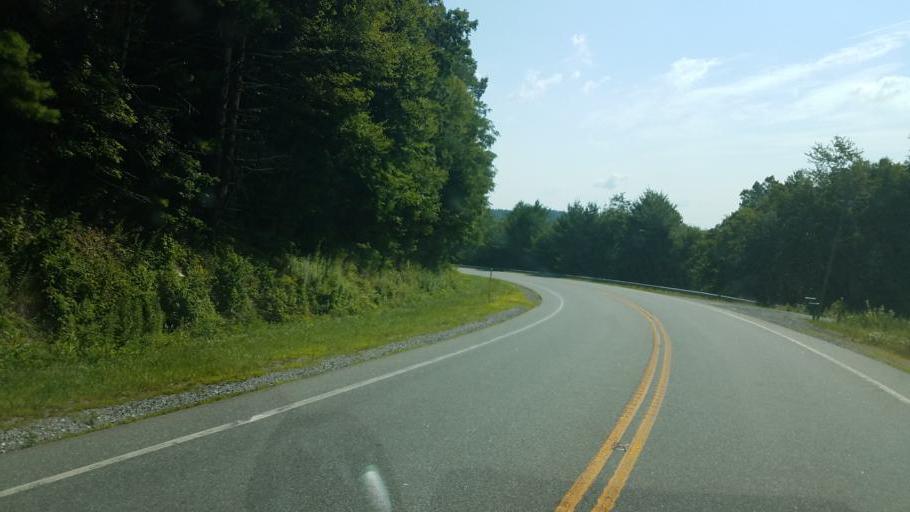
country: US
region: North Carolina
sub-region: Avery County
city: Newland
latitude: 35.9549
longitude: -81.8700
